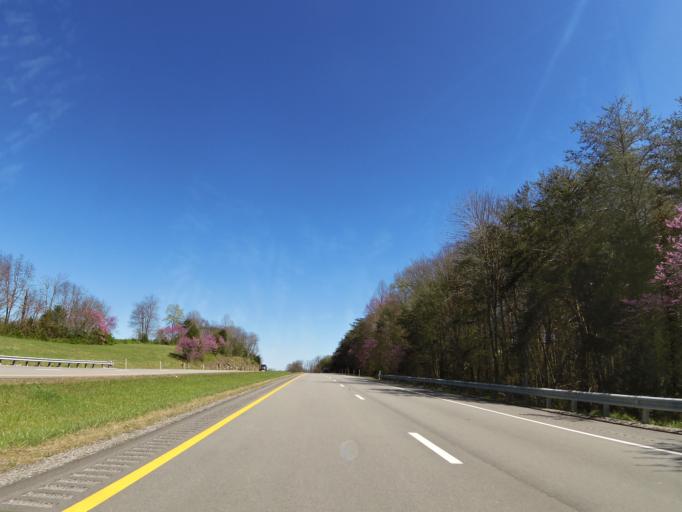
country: US
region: Kentucky
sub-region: Pulaski County
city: Somerset
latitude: 37.0942
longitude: -84.8221
